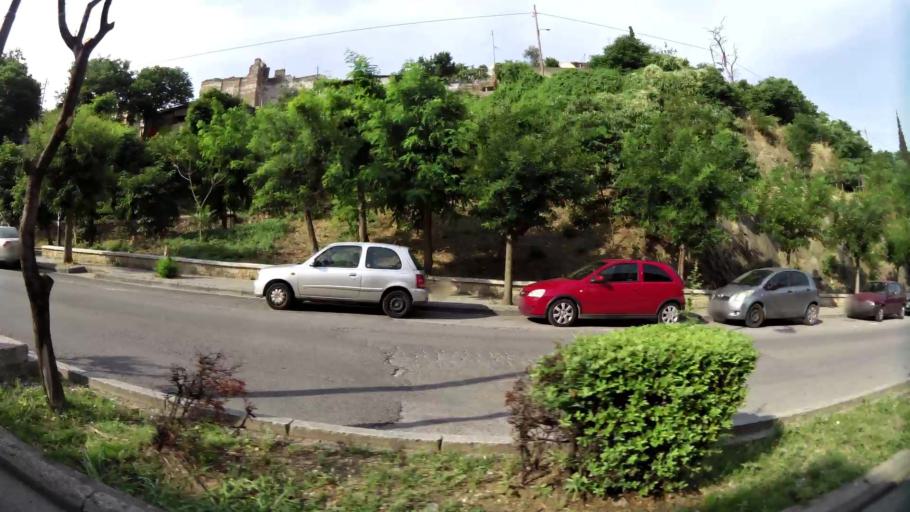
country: GR
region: Central Macedonia
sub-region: Nomos Thessalonikis
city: Sykies
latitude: 40.6452
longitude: 22.9465
